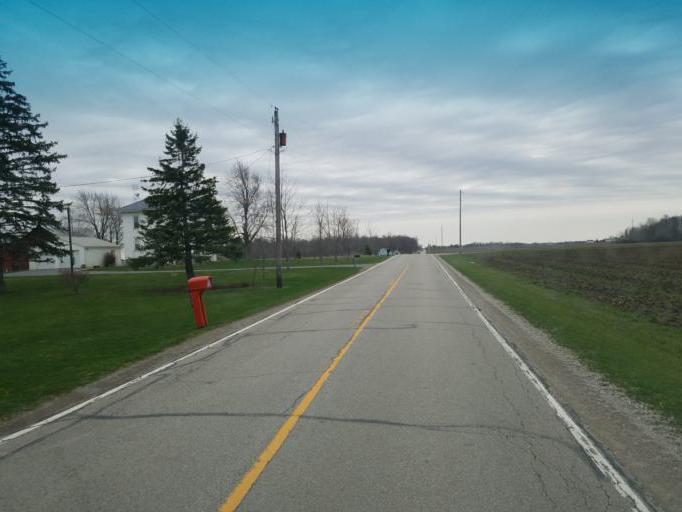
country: US
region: Ohio
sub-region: Crawford County
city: Bucyrus
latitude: 40.8611
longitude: -82.9401
